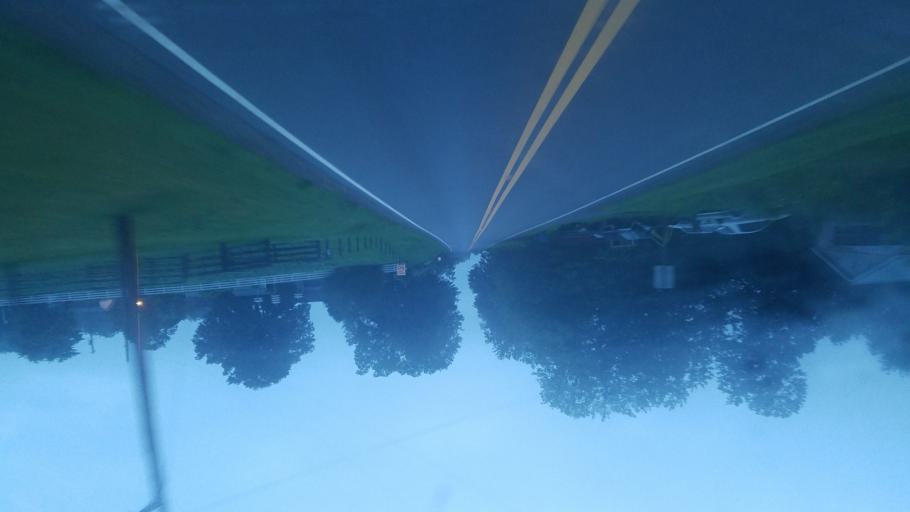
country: US
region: Ohio
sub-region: Knox County
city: Oak Hill
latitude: 40.3363
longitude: -82.0682
